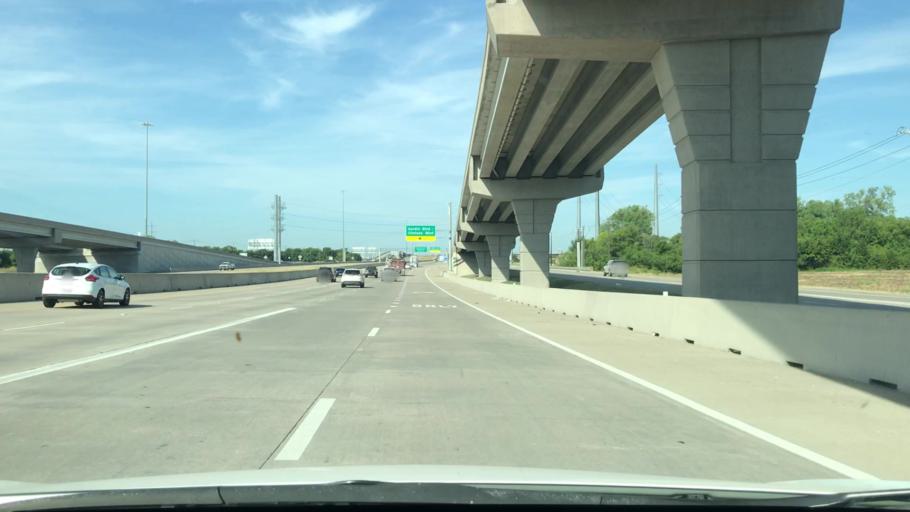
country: US
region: Texas
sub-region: Collin County
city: Fairview
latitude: 33.1561
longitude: -96.6504
